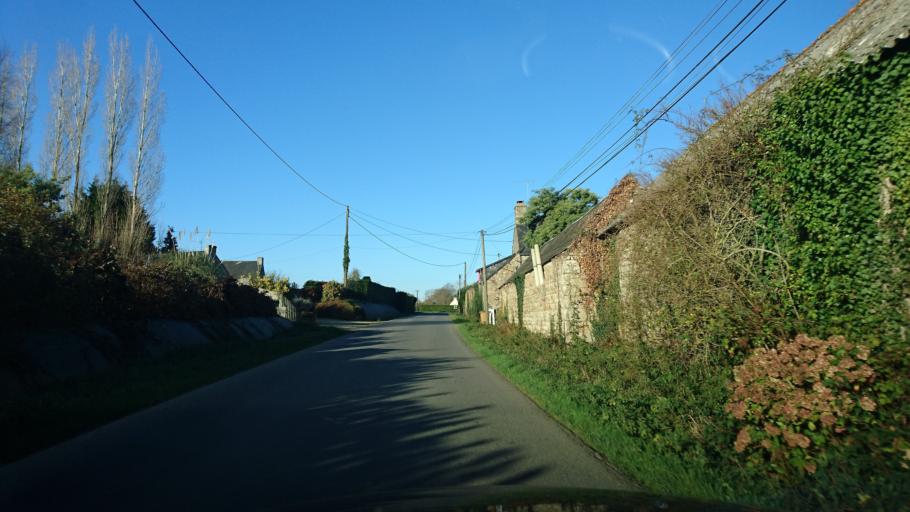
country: FR
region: Brittany
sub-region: Departement des Cotes-d'Armor
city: Pedernec
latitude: 48.5846
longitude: -3.2621
